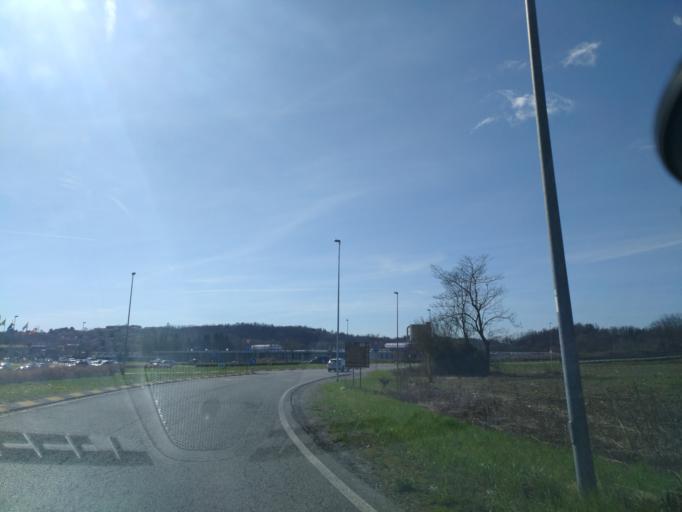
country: IT
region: Lombardy
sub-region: Provincia di Como
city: Anzano del Parco
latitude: 45.7638
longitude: 9.2027
